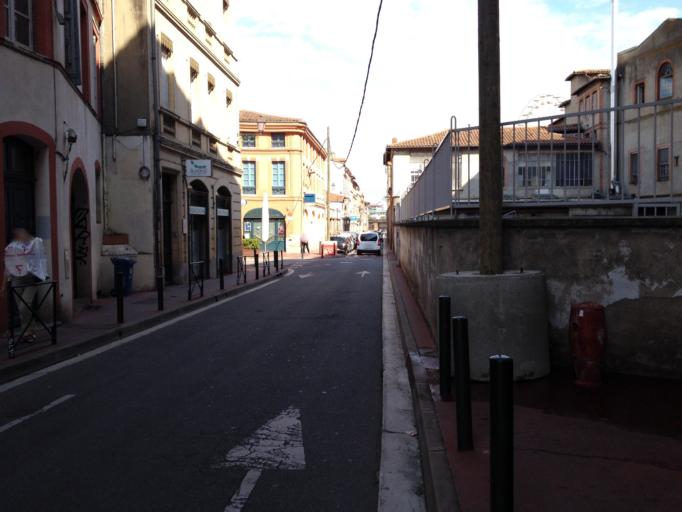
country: FR
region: Midi-Pyrenees
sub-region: Departement de la Haute-Garonne
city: Toulouse
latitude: 43.5992
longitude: 1.4364
